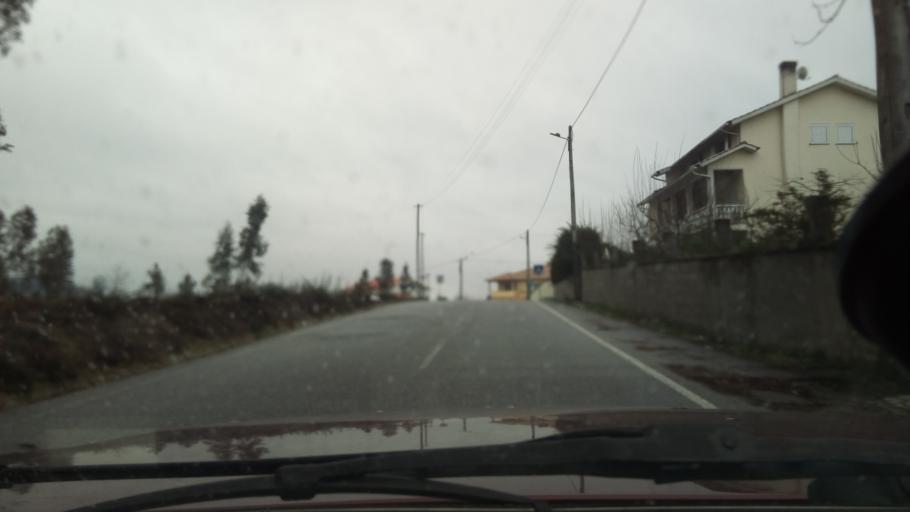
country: PT
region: Viseu
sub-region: Mangualde
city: Mangualde
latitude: 40.5988
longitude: -7.8158
